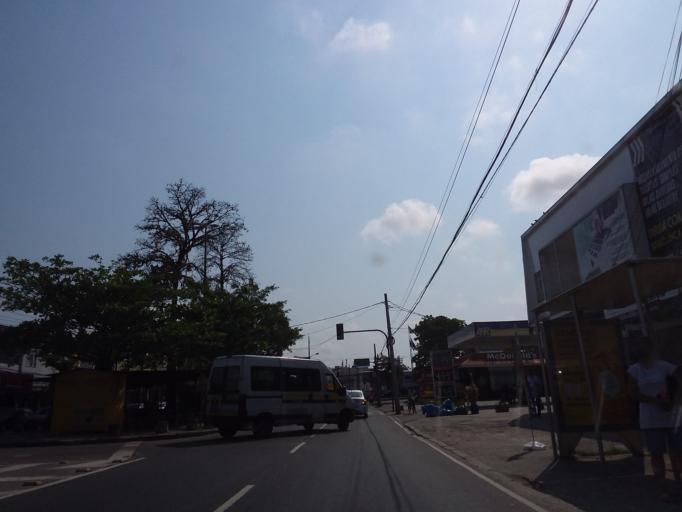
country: BR
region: Rio de Janeiro
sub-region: Nilopolis
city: Nilopolis
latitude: -22.9023
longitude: -43.5492
